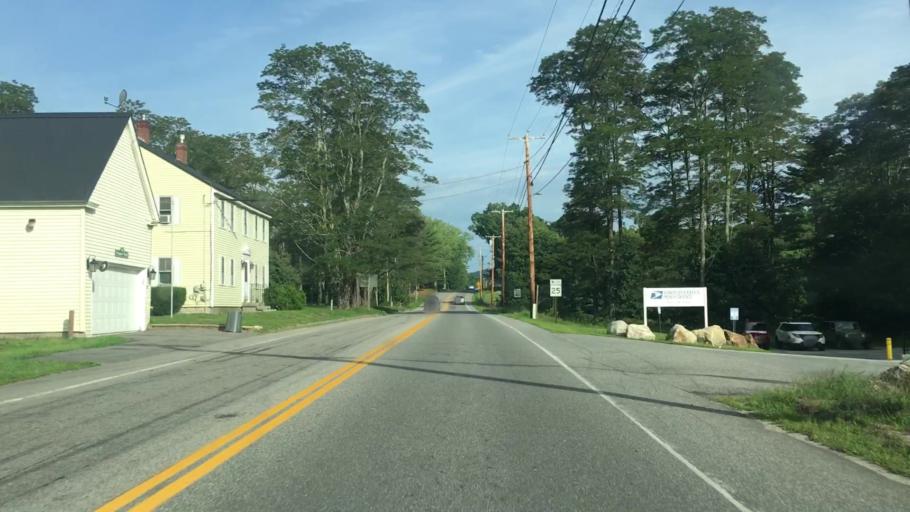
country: US
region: Maine
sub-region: York County
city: Limington
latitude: 43.7474
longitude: -70.6796
